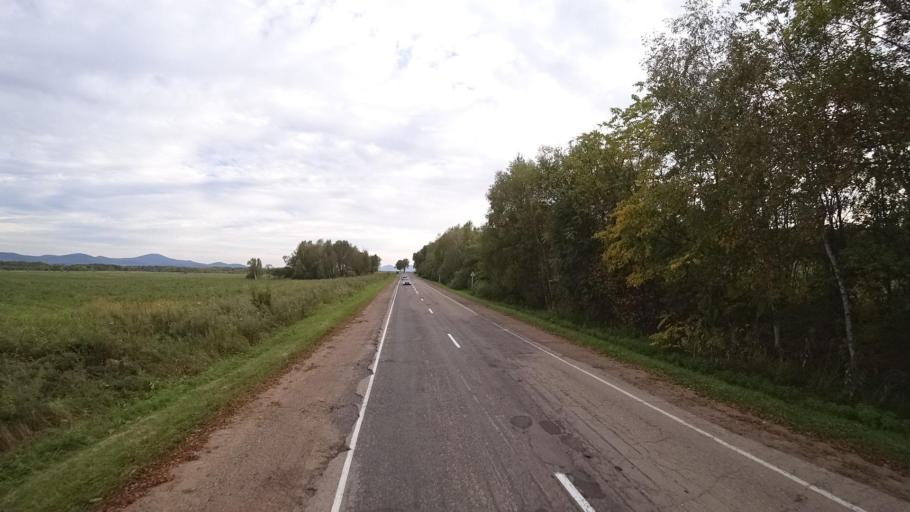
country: RU
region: Primorskiy
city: Dostoyevka
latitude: 44.3653
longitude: 133.4332
